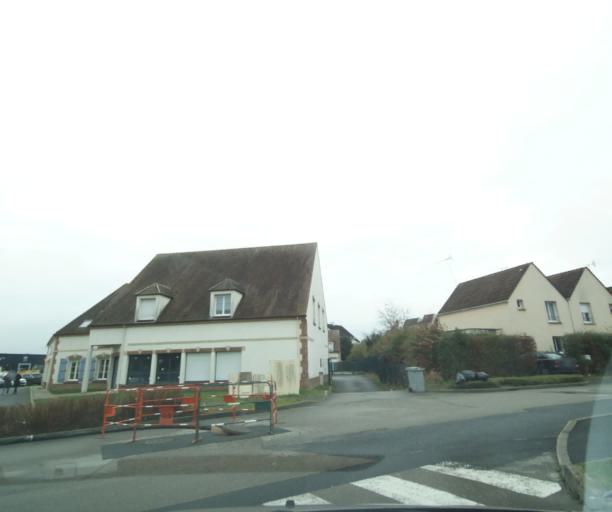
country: FR
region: Picardie
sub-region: Departement de l'Oise
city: Noyon
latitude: 49.5747
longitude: 2.9888
